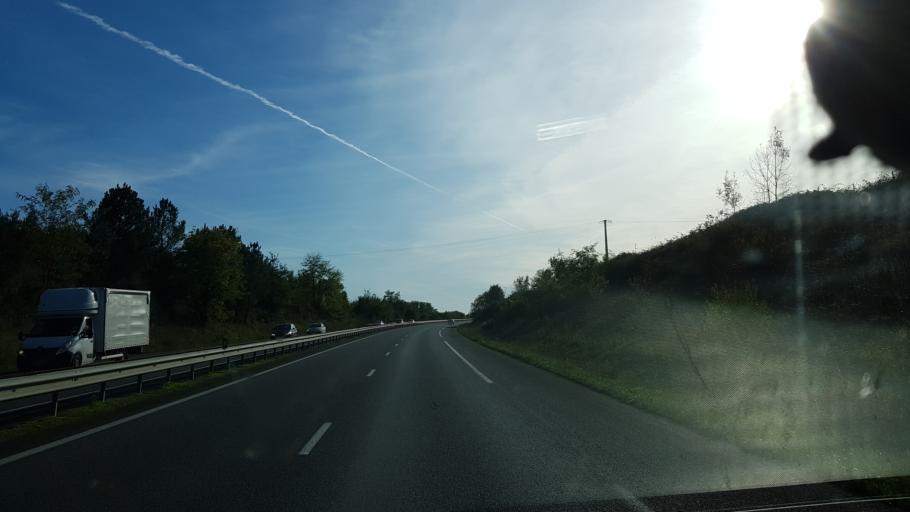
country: FR
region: Poitou-Charentes
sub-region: Departement de la Charente-Maritime
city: Montlieu-la-Garde
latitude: 45.2669
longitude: -0.2476
